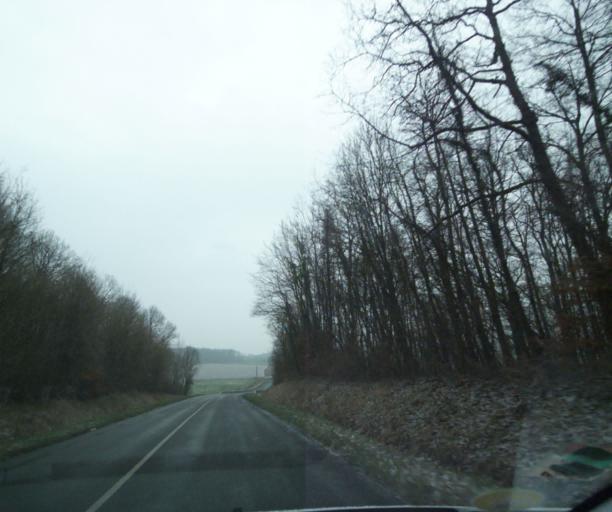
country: FR
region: Champagne-Ardenne
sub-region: Departement de la Haute-Marne
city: Wassy
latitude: 48.4714
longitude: 5.0222
